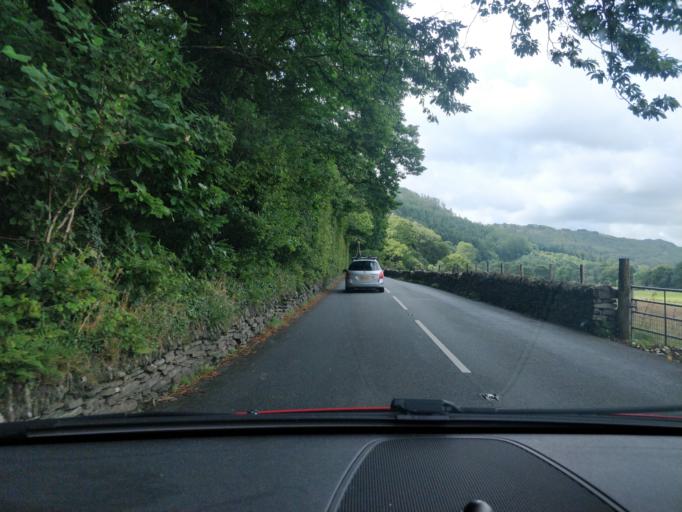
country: GB
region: Wales
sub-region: Gwynedd
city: Ffestiniog
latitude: 52.9597
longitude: -3.9526
